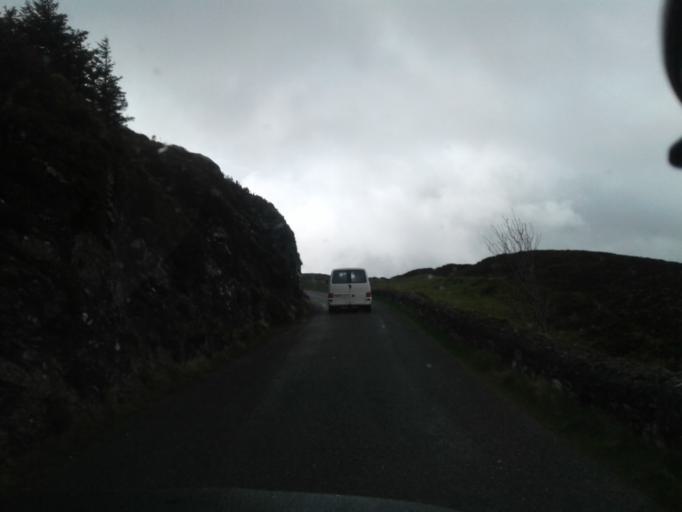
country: IE
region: Leinster
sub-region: Wicklow
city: Enniskerry
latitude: 53.1079
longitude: -6.2569
